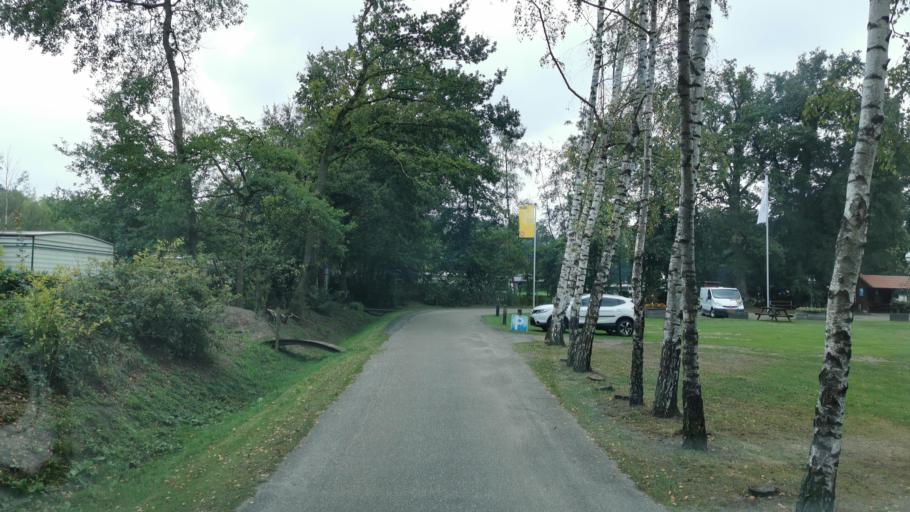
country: NL
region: Overijssel
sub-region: Gemeente Losser
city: Losser
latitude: 52.3215
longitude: 7.0272
